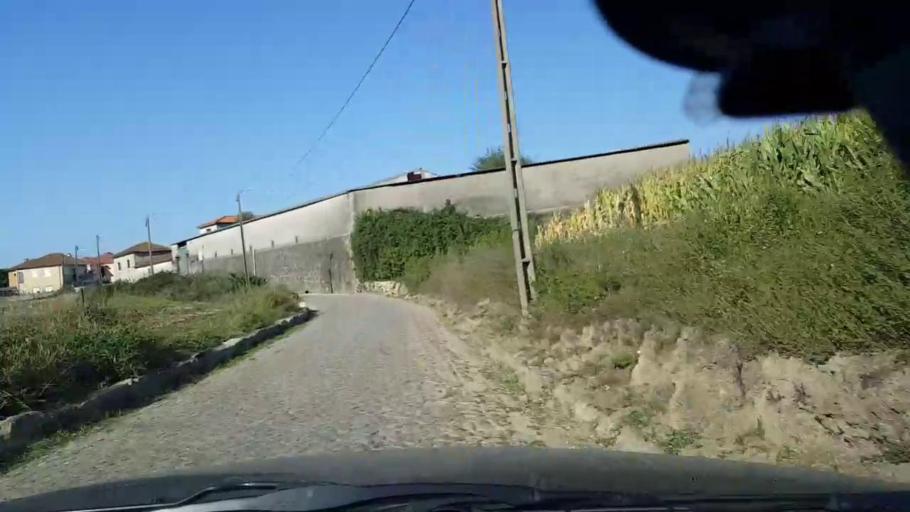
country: PT
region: Porto
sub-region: Vila do Conde
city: Arvore
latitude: 41.3550
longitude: -8.7183
